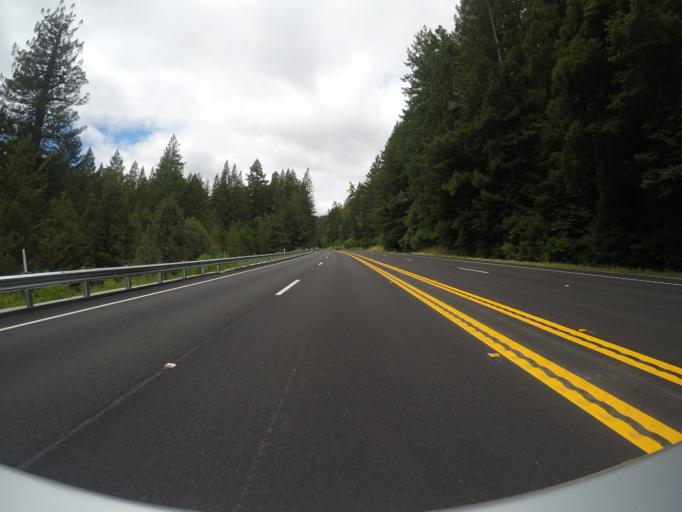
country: US
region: California
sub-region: Humboldt County
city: Redway
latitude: 40.3333
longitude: -123.9288
